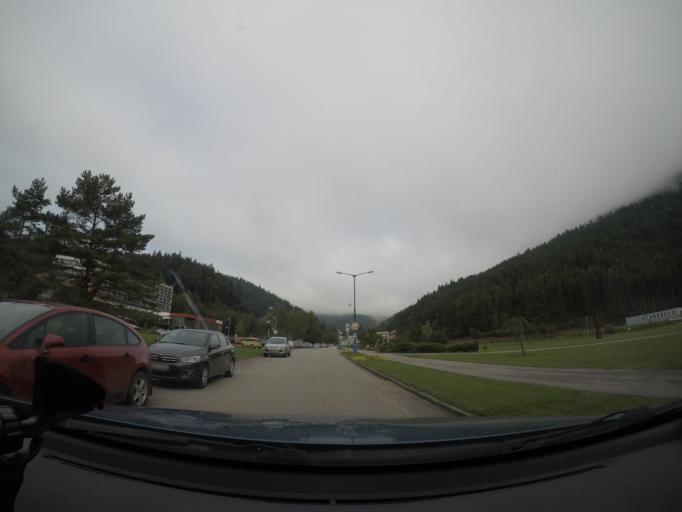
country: SK
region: Zilinsky
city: Ruzomberok
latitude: 49.1320
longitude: 19.4000
